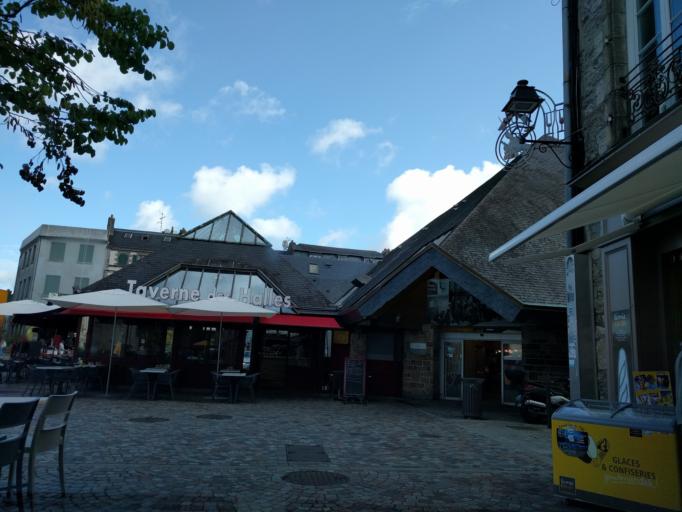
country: FR
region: Brittany
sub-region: Departement du Finistere
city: Quimper
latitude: 47.9952
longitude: -4.1055
